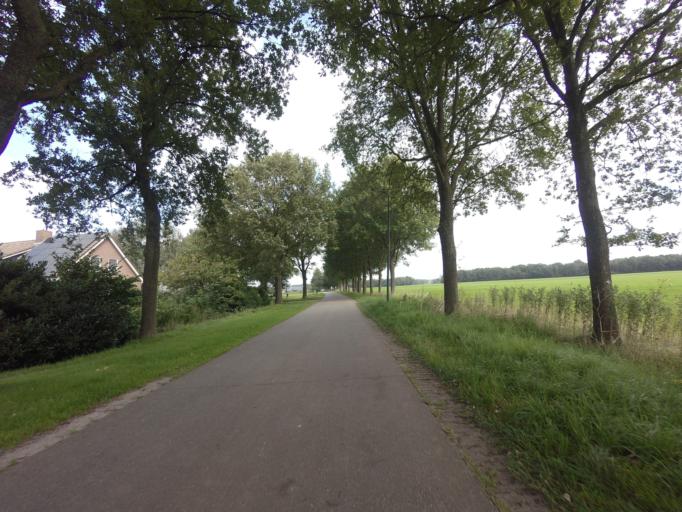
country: NL
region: Drenthe
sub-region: Gemeente Westerveld
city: Havelte
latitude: 52.8415
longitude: 6.2358
